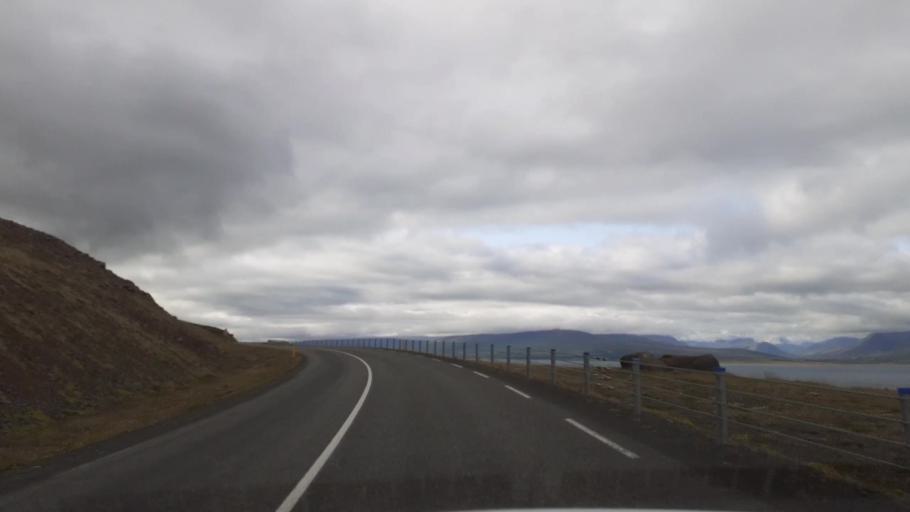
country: IS
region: Northeast
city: Akureyri
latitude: 65.8322
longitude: -18.0573
